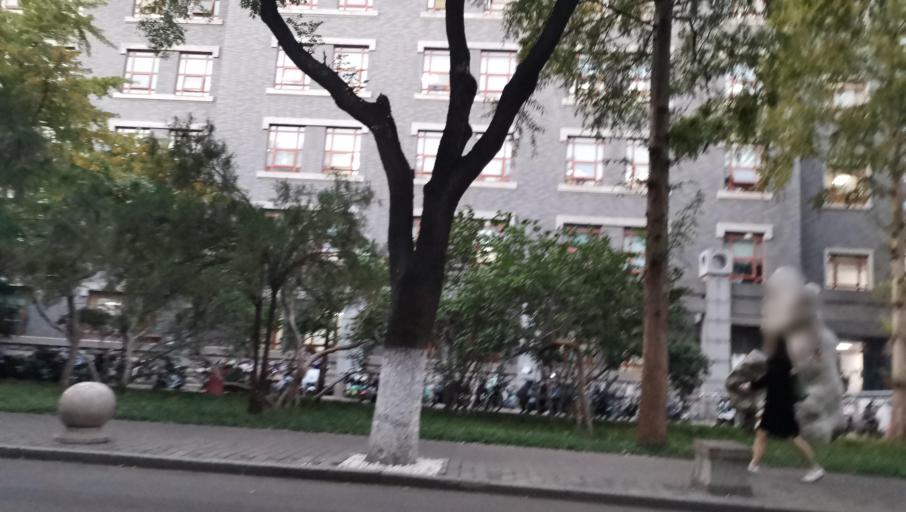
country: CN
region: Shandong Sheng
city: Jinan
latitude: 36.6538
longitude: 117.0134
